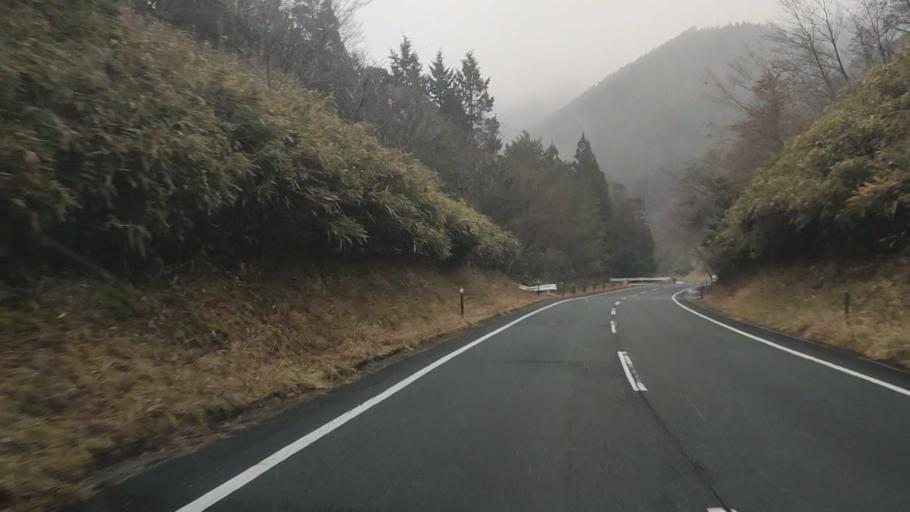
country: JP
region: Kumamoto
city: Matsubase
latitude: 32.5691
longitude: 130.9097
